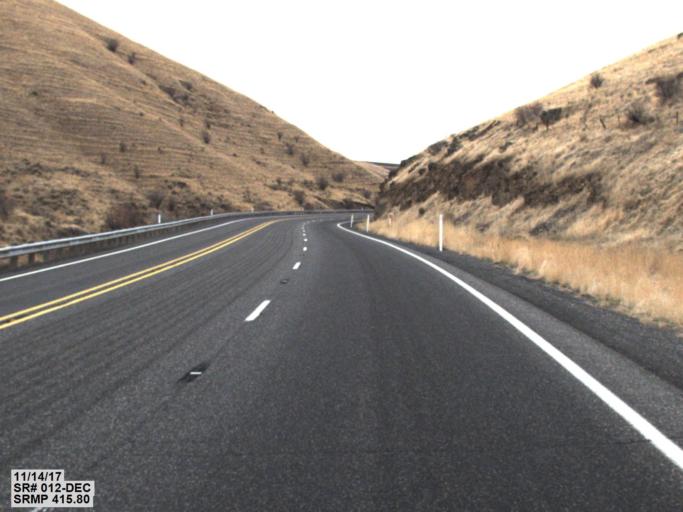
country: US
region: Washington
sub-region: Garfield County
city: Pomeroy
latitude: 46.4420
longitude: -117.3796
